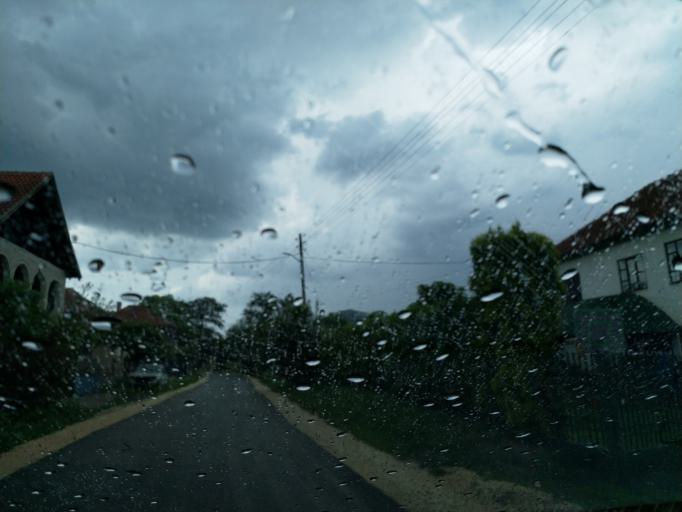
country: RS
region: Central Serbia
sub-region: Borski Okrug
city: Bor
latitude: 44.0142
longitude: 21.9834
